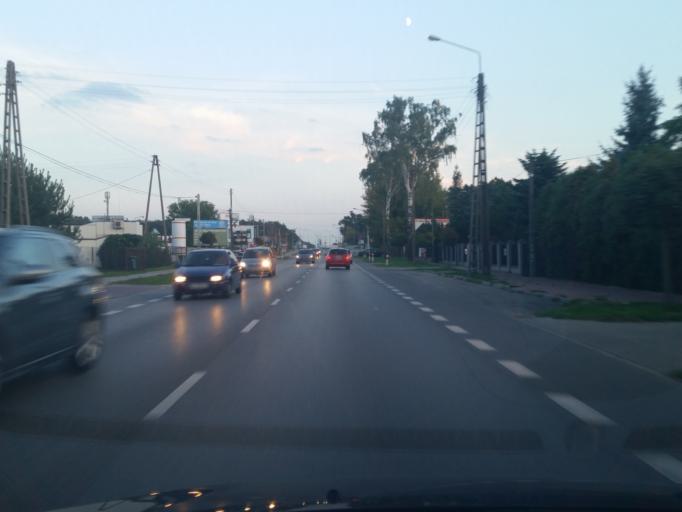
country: PL
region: Masovian Voivodeship
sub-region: Powiat legionowski
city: Jablonna
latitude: 52.3661
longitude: 20.9325
